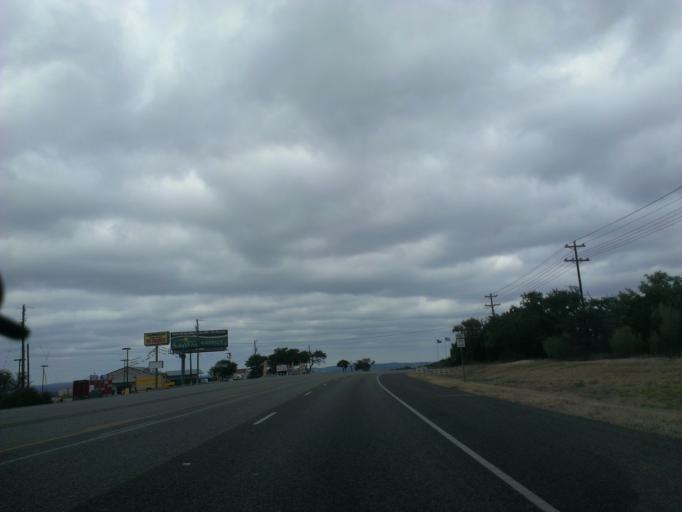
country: US
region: Texas
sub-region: Travis County
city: Briarcliff
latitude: 30.3565
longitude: -98.0674
